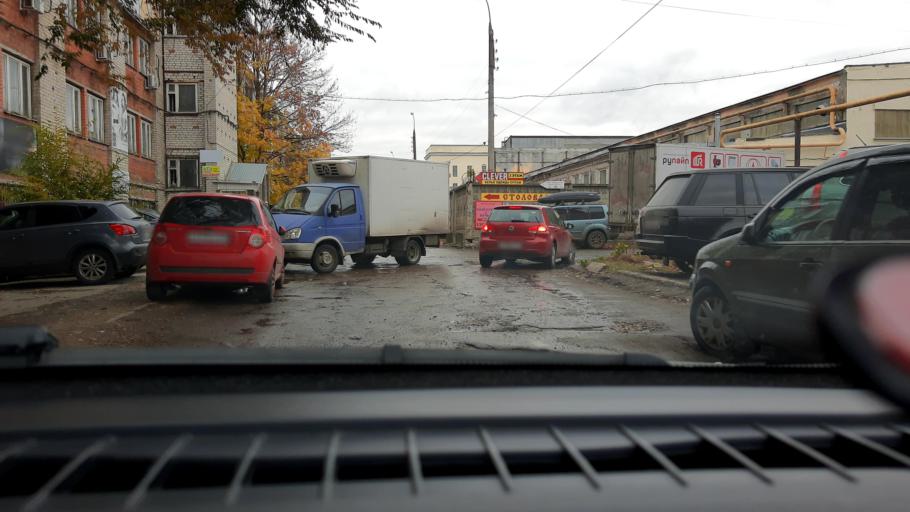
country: RU
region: Nizjnij Novgorod
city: Nizhniy Novgorod
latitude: 56.2690
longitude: 43.9396
